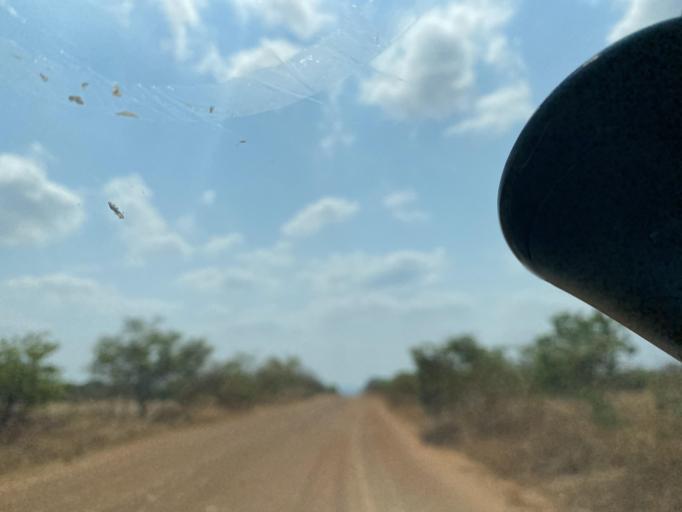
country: ZM
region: Lusaka
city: Chongwe
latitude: -15.5921
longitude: 28.7885
